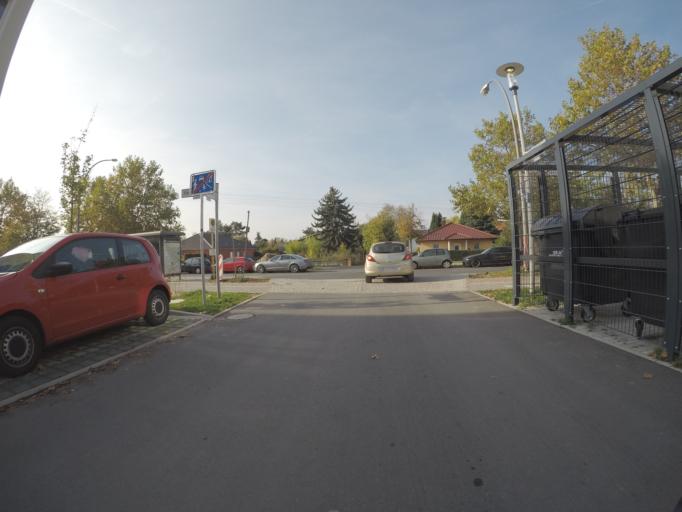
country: DE
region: Berlin
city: Altglienicke
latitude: 52.4132
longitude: 13.5295
